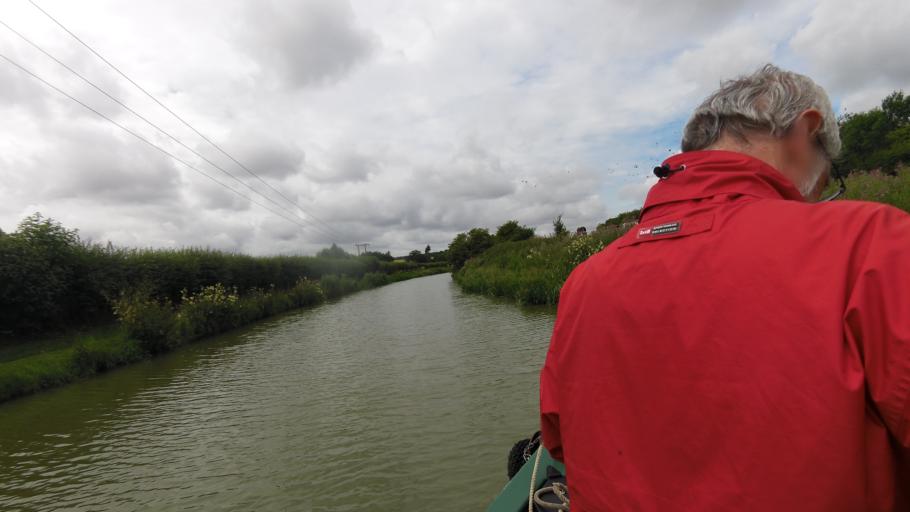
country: GB
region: England
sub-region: Wiltshire
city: Great Bedwyn
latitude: 51.3584
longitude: -1.6252
